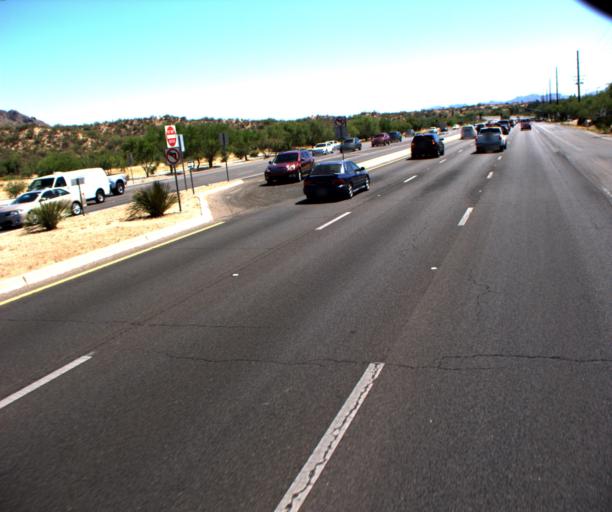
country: US
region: Arizona
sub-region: Pima County
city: Oro Valley
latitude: 32.3982
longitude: -110.9574
